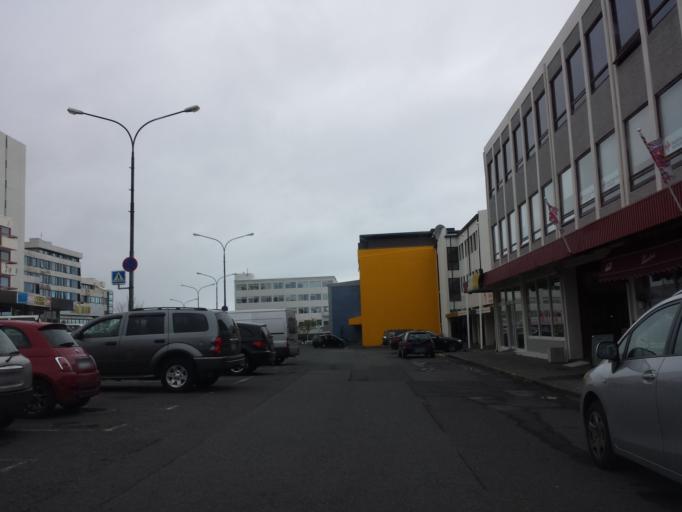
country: IS
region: Capital Region
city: Kopavogur
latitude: 64.1125
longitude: -21.9020
